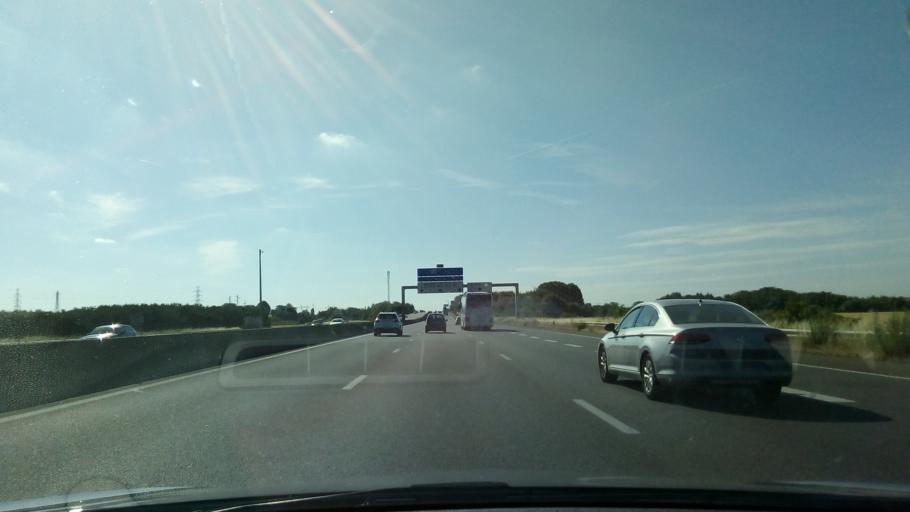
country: FR
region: Ile-de-France
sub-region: Departement de Seine-et-Marne
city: Nandy
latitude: 48.6126
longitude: 2.5686
